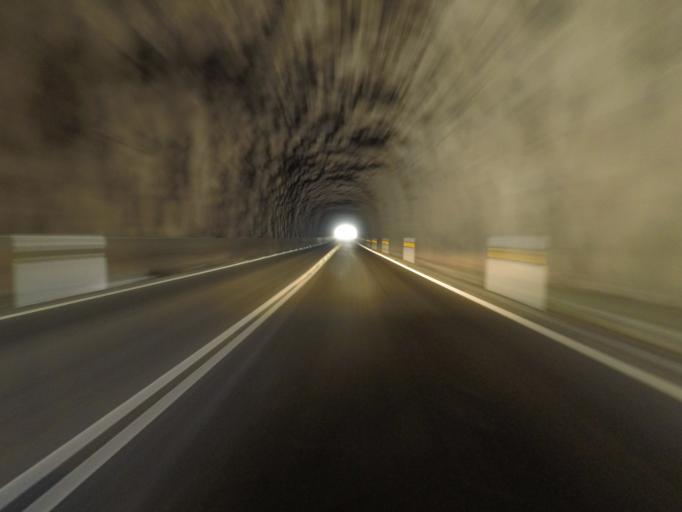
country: ES
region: Canary Islands
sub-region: Provincia de Santa Cruz de Tenerife
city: Alajero
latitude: 28.0328
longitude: -17.2001
